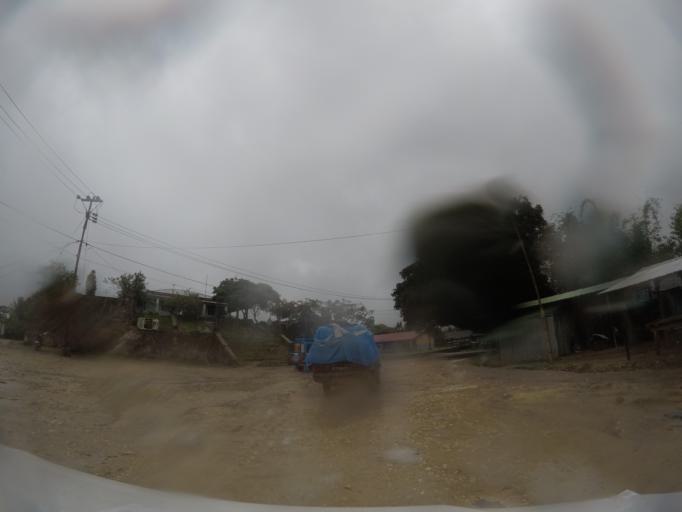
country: TL
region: Baucau
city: Venilale
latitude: -8.6437
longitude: 126.3784
